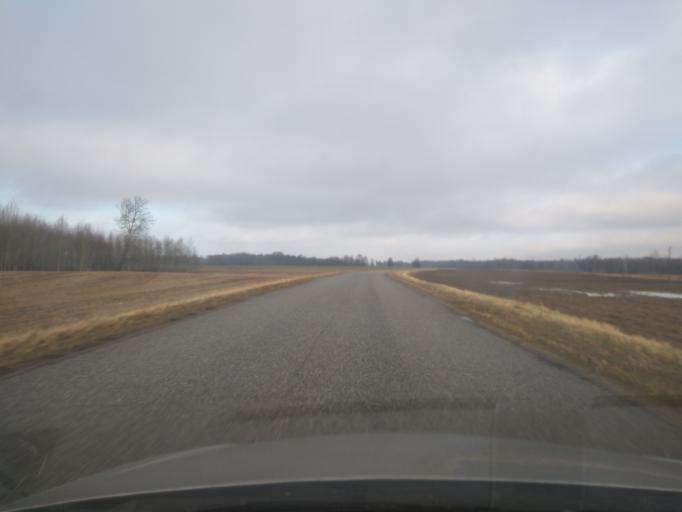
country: LV
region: Saldus Rajons
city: Saldus
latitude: 56.7715
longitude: 22.3869
